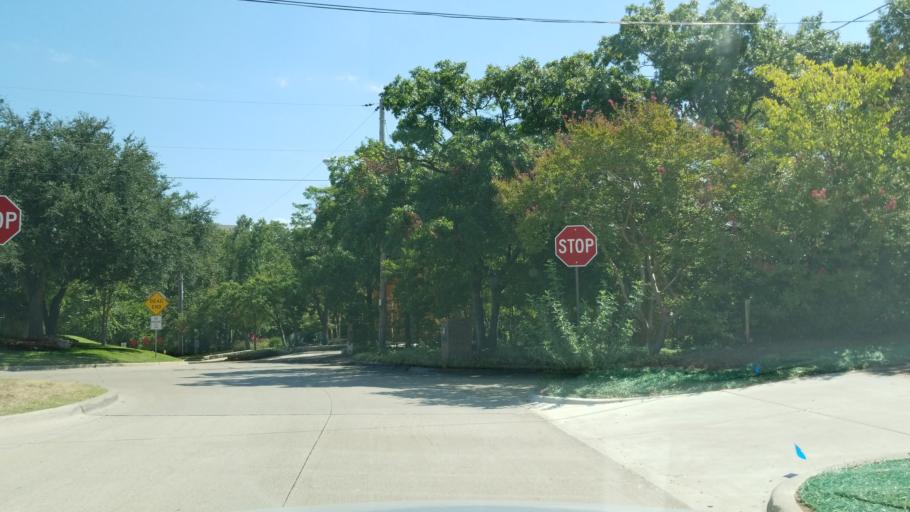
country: US
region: Texas
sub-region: Dallas County
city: Addison
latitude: 32.9466
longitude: -96.8108
